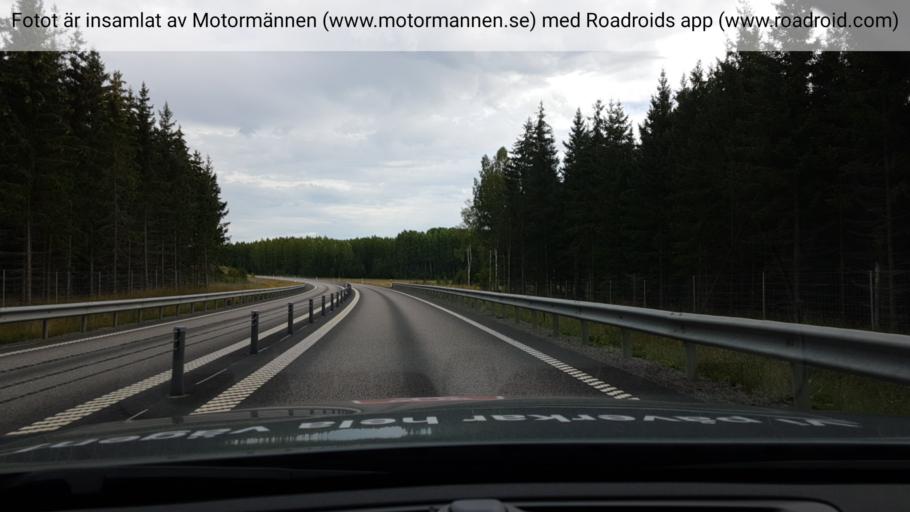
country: SE
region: Uppsala
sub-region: Heby Kommun
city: Heby
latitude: 59.9786
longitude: 16.8507
